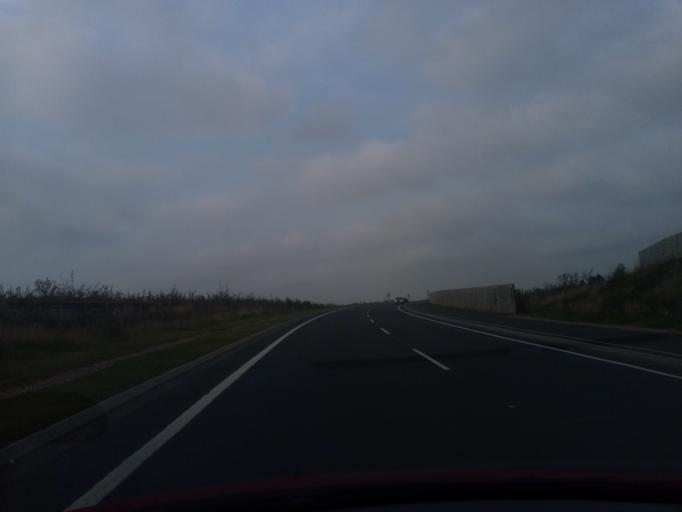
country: GB
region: England
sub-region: Leicestershire
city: Kegworth
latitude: 52.8323
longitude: -1.2945
